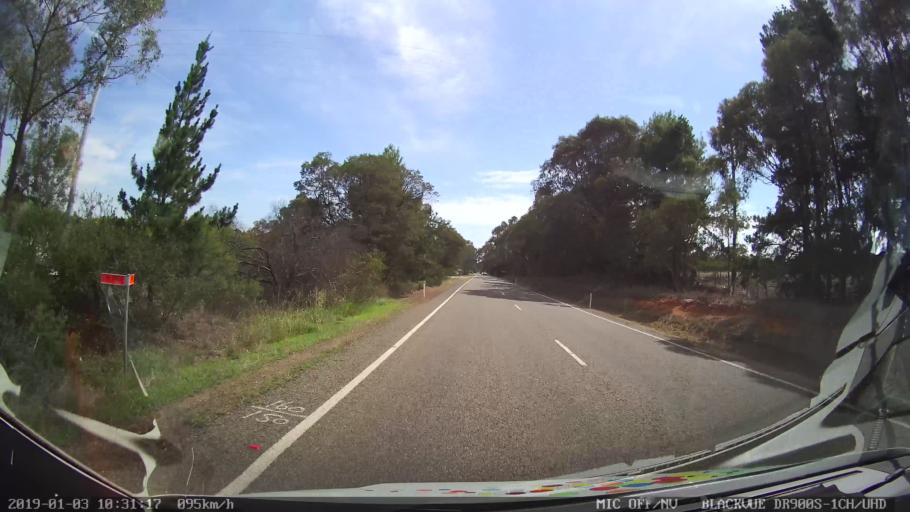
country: AU
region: New South Wales
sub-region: Young
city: Young
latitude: -34.3520
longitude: 148.2757
